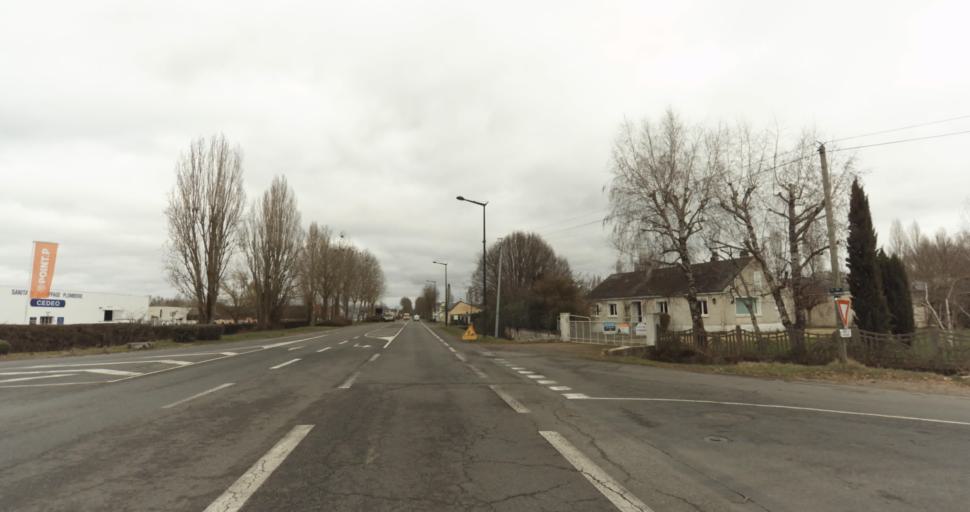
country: FR
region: Pays de la Loire
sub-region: Departement de Maine-et-Loire
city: Saumur
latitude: 47.2785
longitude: -0.0569
